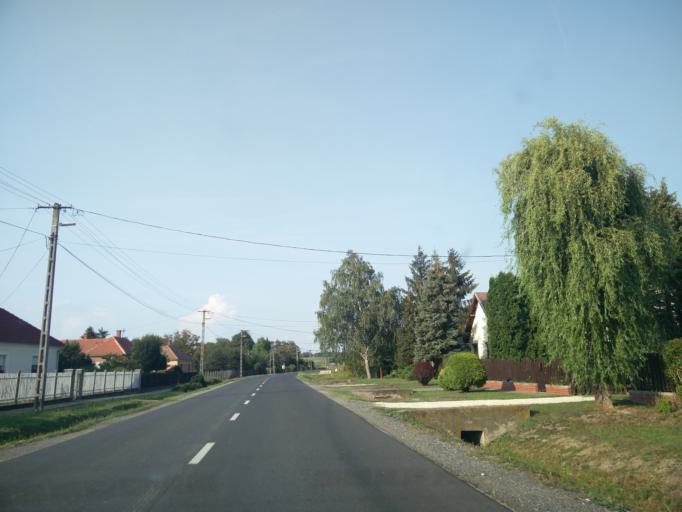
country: HU
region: Zala
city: Zalaegerszeg
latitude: 46.9071
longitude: 16.9455
